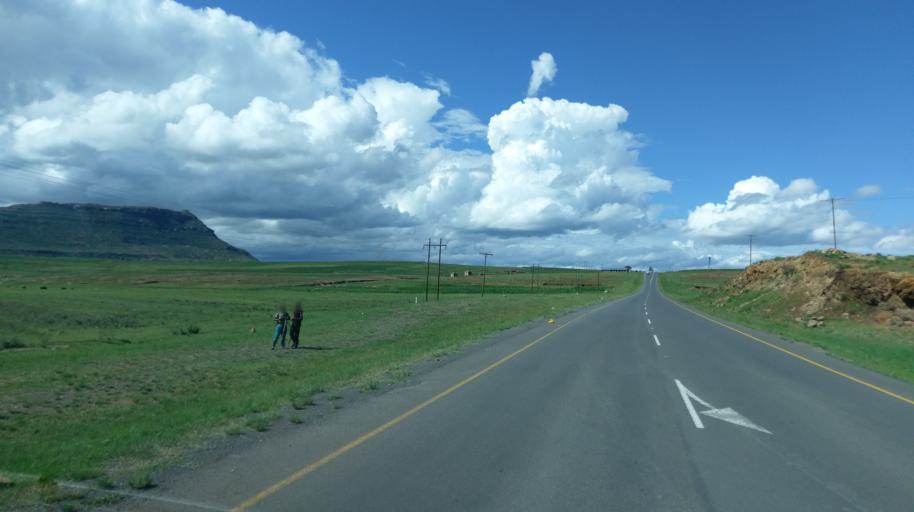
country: LS
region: Maseru
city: Maseru
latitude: -29.5497
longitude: 27.4986
